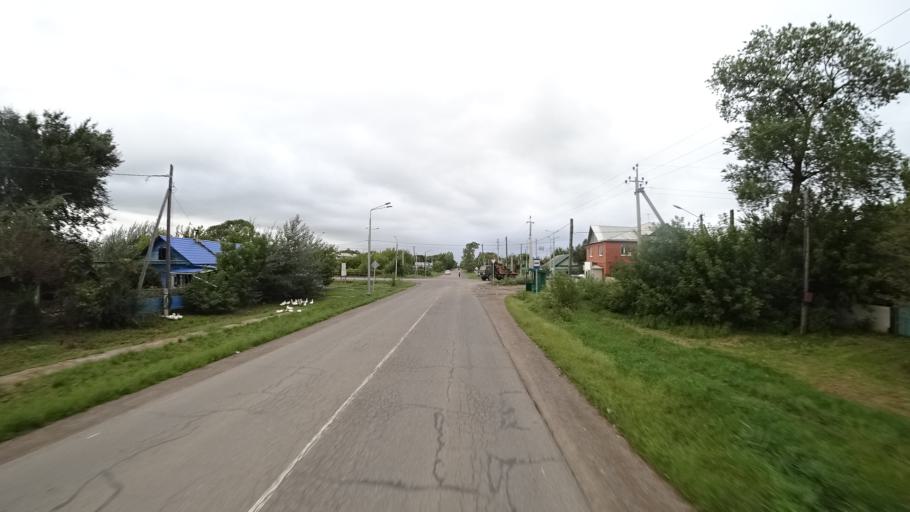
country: RU
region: Primorskiy
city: Chernigovka
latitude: 44.3385
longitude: 132.5870
